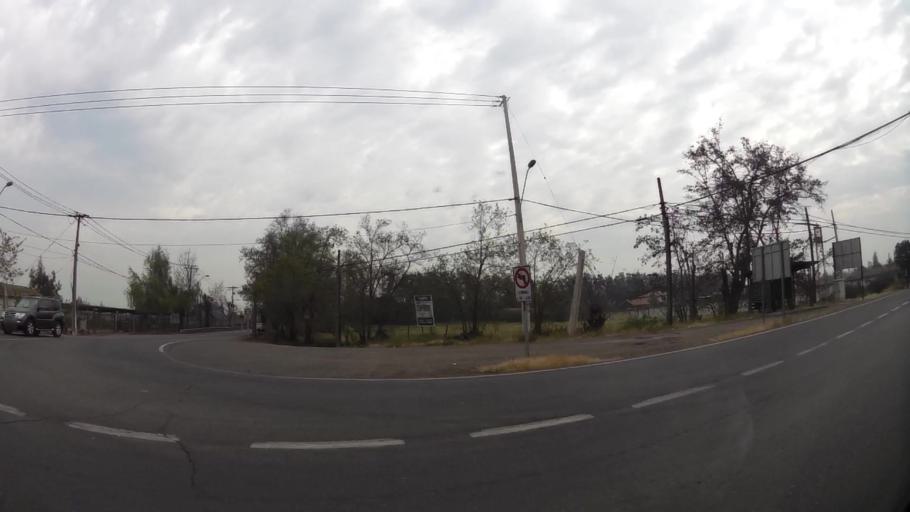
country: CL
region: Santiago Metropolitan
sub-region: Provincia de Chacabuco
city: Chicureo Abajo
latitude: -33.2515
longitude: -70.7173
